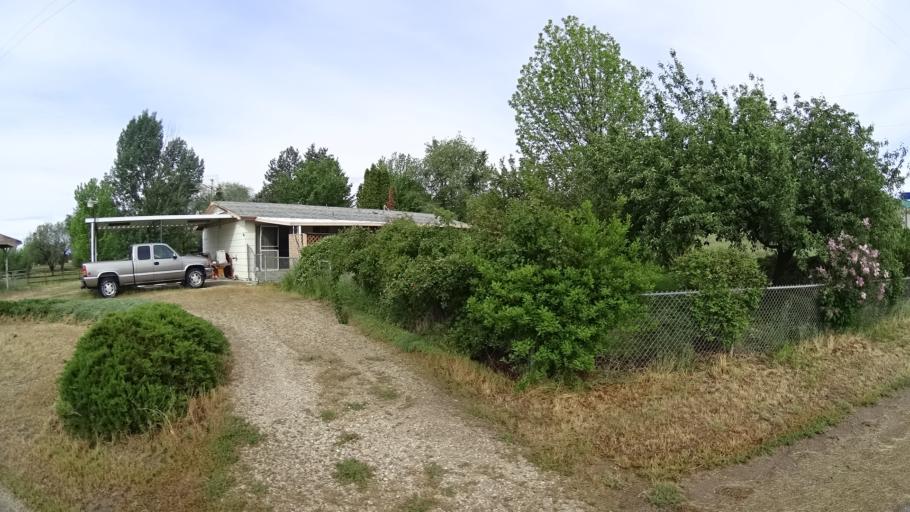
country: US
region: Idaho
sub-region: Ada County
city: Eagle
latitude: 43.7300
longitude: -116.3192
